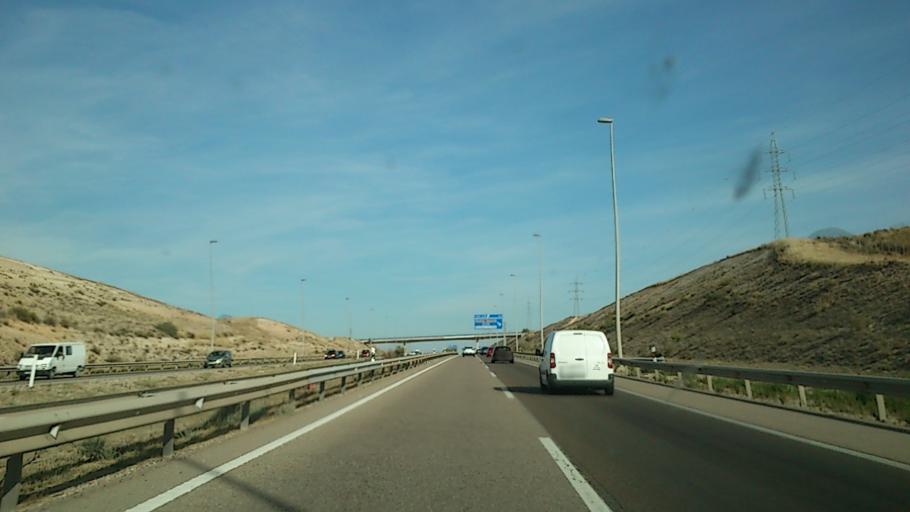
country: ES
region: Aragon
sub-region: Provincia de Zaragoza
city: Cuarte de Huerva
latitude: 41.6070
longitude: -0.9075
